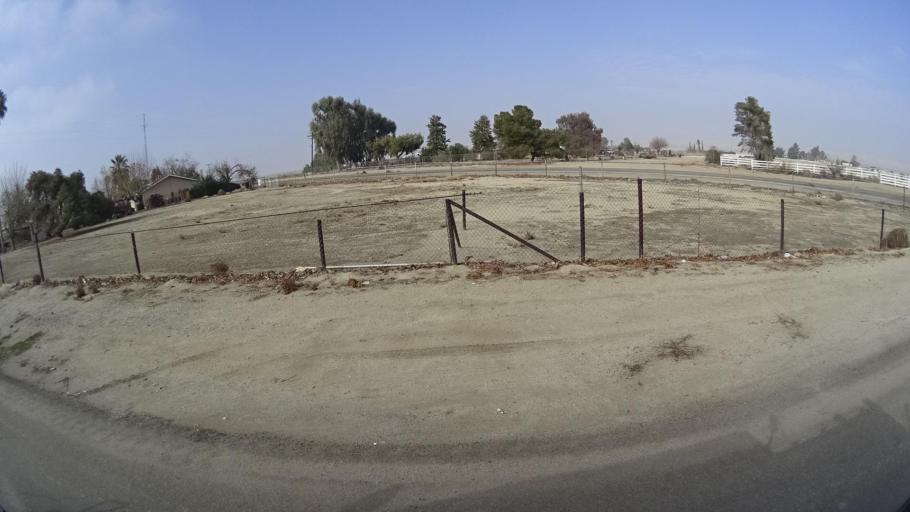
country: US
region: California
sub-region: Kern County
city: Ford City
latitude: 35.2094
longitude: -119.4089
